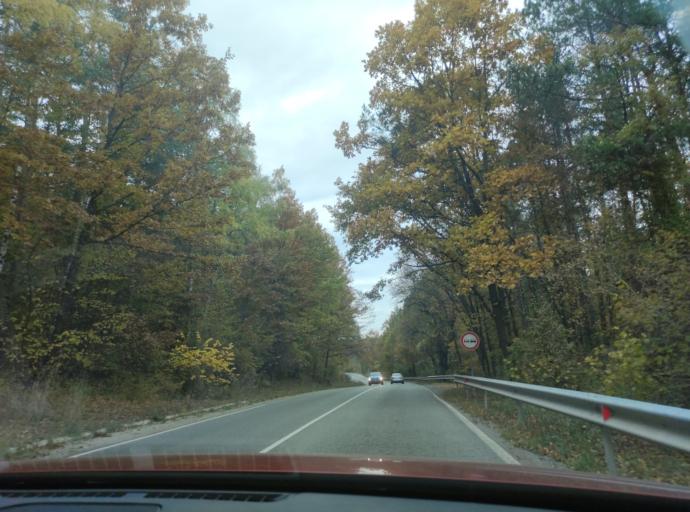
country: BG
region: Sofiya
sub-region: Obshtina Godech
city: Godech
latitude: 42.9796
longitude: 23.1362
